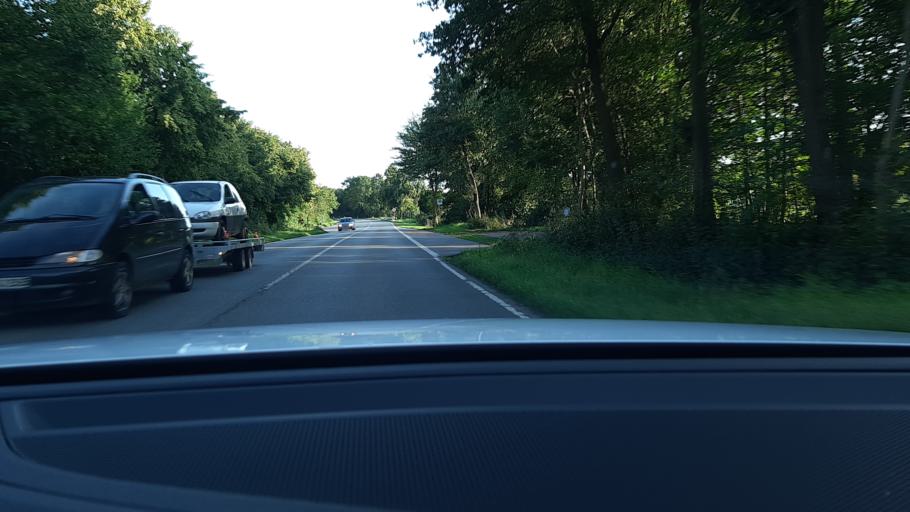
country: DE
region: Schleswig-Holstein
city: Stockelsdorf
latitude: 53.9105
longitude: 10.6406
